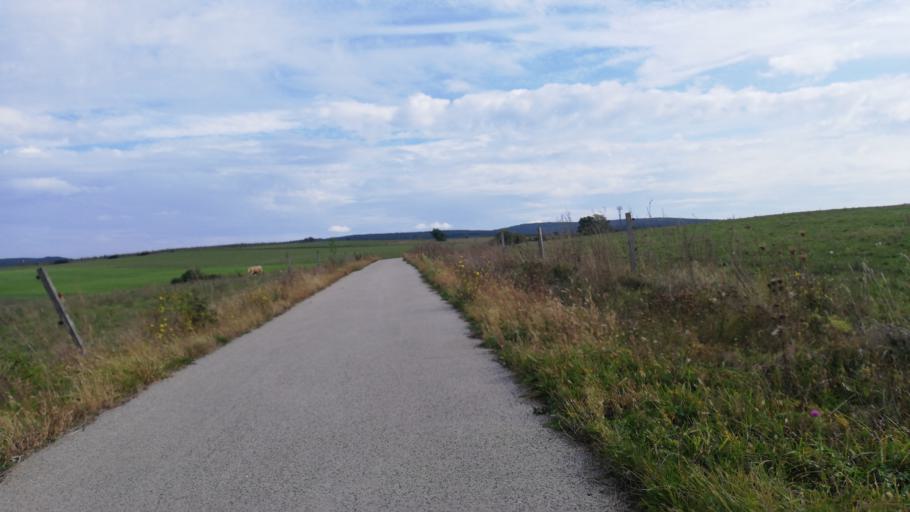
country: CZ
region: South Moravian
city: Sudomerice
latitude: 48.8427
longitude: 17.2795
